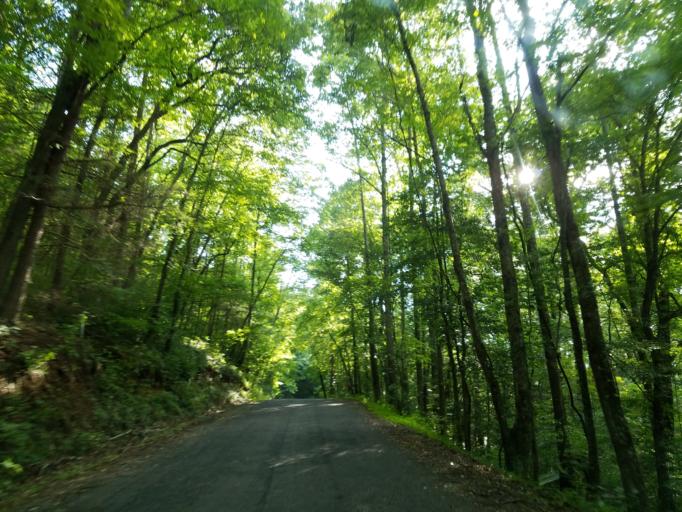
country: US
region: Georgia
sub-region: Gilmer County
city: Ellijay
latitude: 34.6308
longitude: -84.2587
